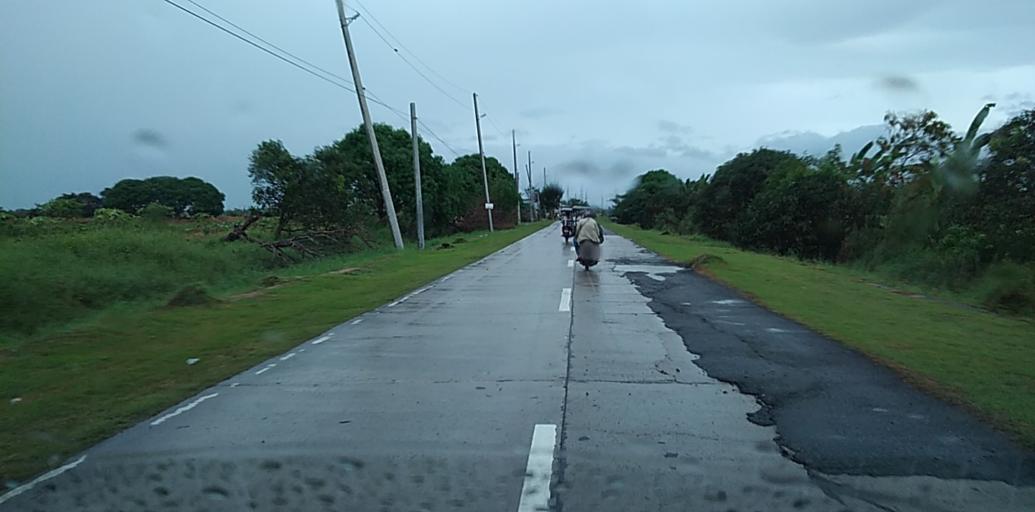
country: PH
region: Central Luzon
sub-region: Province of Pampanga
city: Salapungan
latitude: 15.1335
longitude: 120.8986
